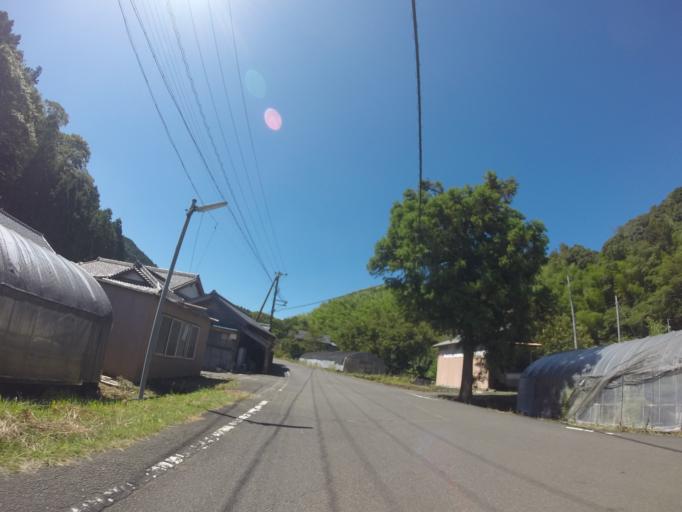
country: JP
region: Shizuoka
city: Fujieda
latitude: 34.9146
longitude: 138.1847
